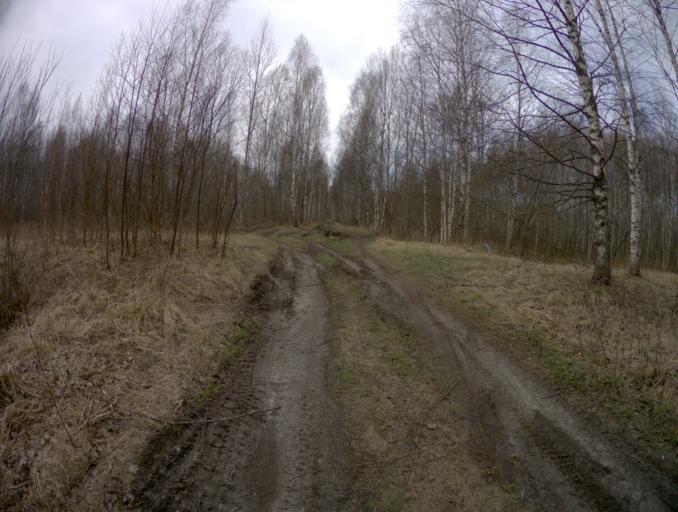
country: RU
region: Vladimir
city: Raduzhnyy
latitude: 55.9127
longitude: 40.2452
